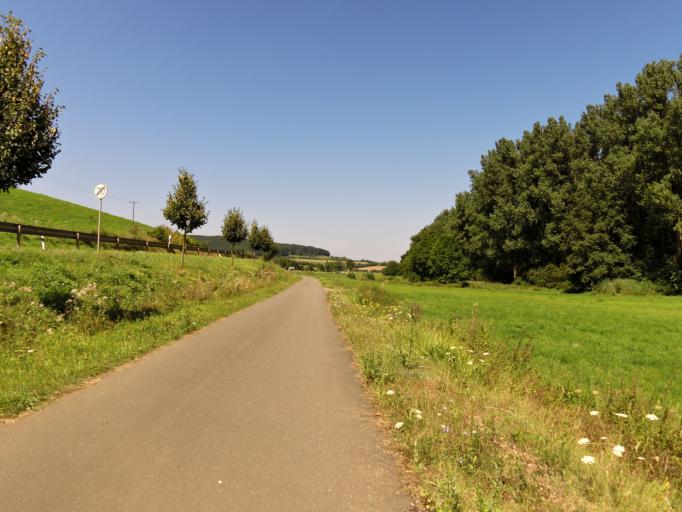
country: DE
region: Rheinland-Pfalz
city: Munchweiler an der Alsenz
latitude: 49.5295
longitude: 7.8866
